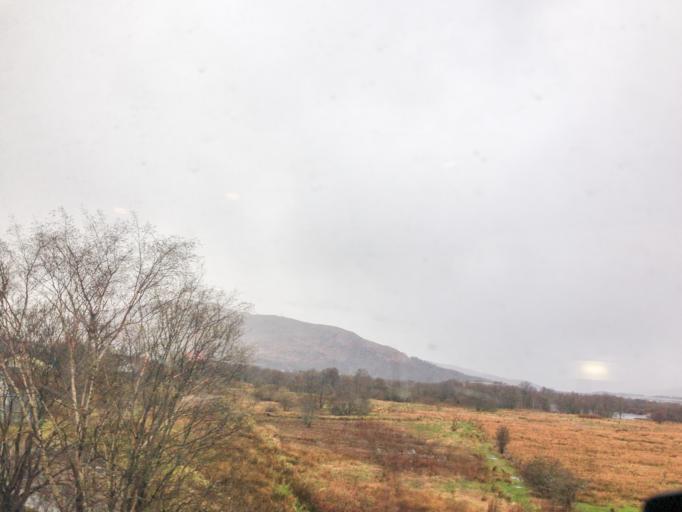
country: GB
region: Scotland
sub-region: Highland
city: Fort William
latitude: 56.8287
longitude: -5.0872
